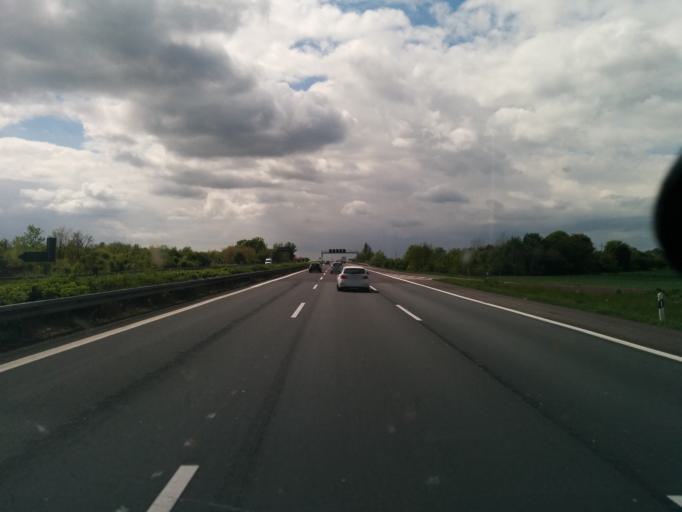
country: DE
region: Saxony-Anhalt
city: Hohenwarthe
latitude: 52.2222
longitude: 11.7152
